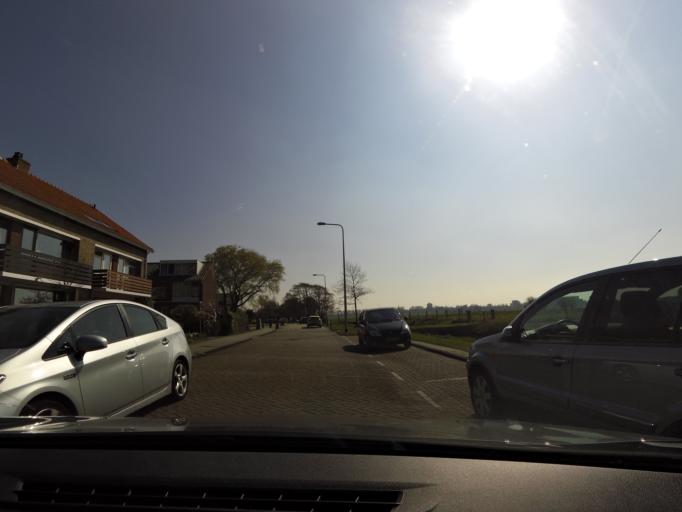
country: NL
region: South Holland
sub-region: Gemeente Maassluis
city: Maassluis
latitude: 51.9377
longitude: 4.2661
